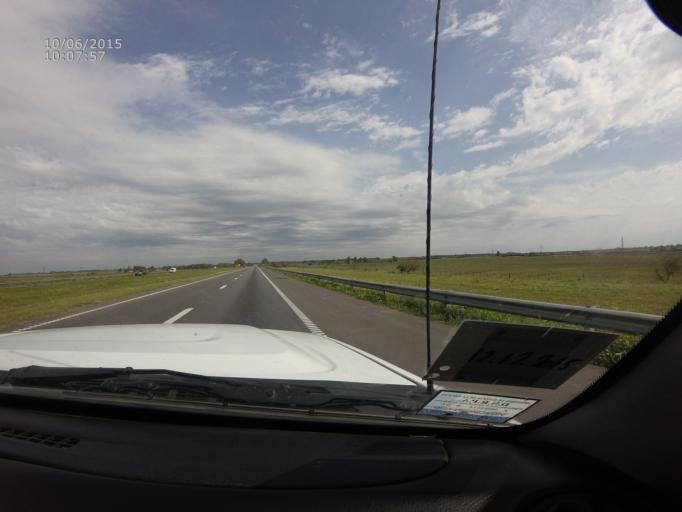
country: AR
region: Buenos Aires
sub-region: Partido de Baradero
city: Baradero
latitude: -33.8123
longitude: -59.6008
